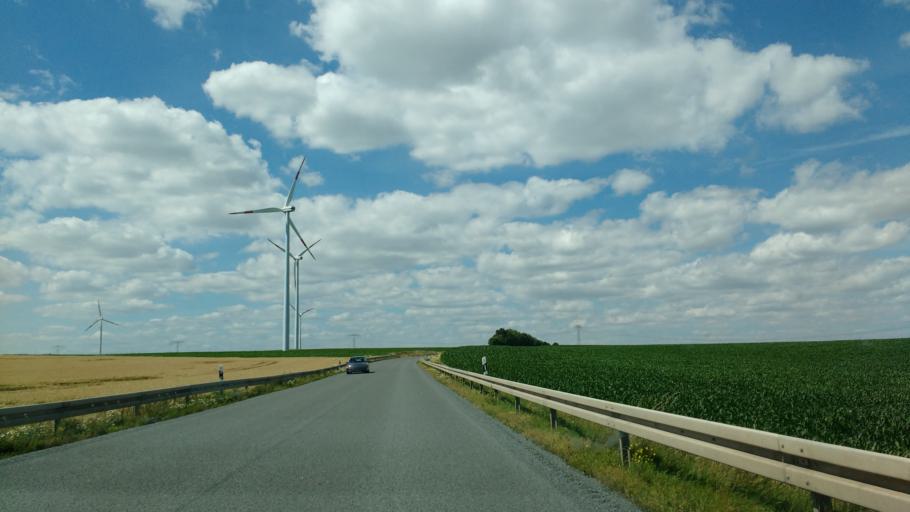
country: DE
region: Saxony-Anhalt
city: Farnstadt
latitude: 51.4079
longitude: 11.5819
